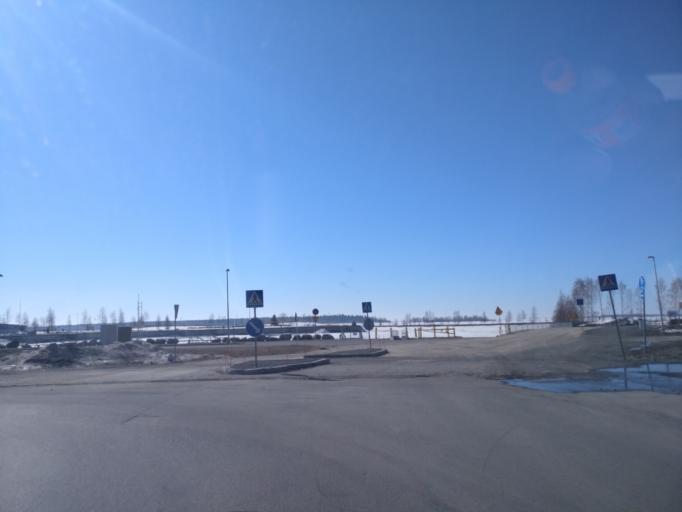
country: FI
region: Lapland
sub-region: Kemi-Tornio
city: Kemi
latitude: 65.7368
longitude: 24.5541
